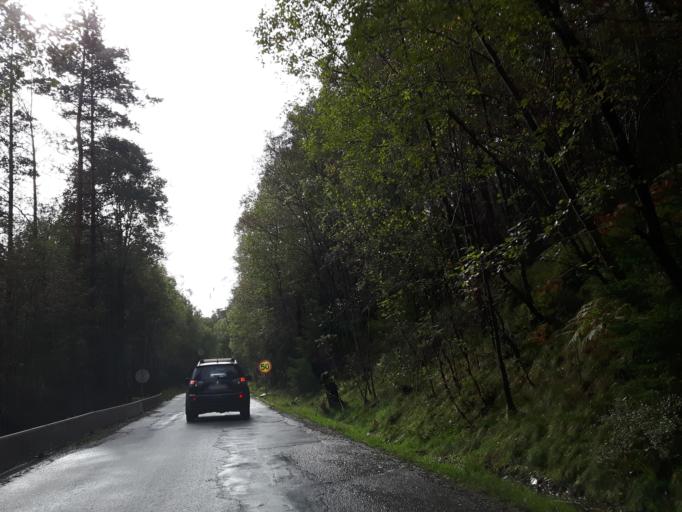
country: NO
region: Rogaland
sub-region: Lund
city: Moi
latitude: 58.3976
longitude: 6.6284
